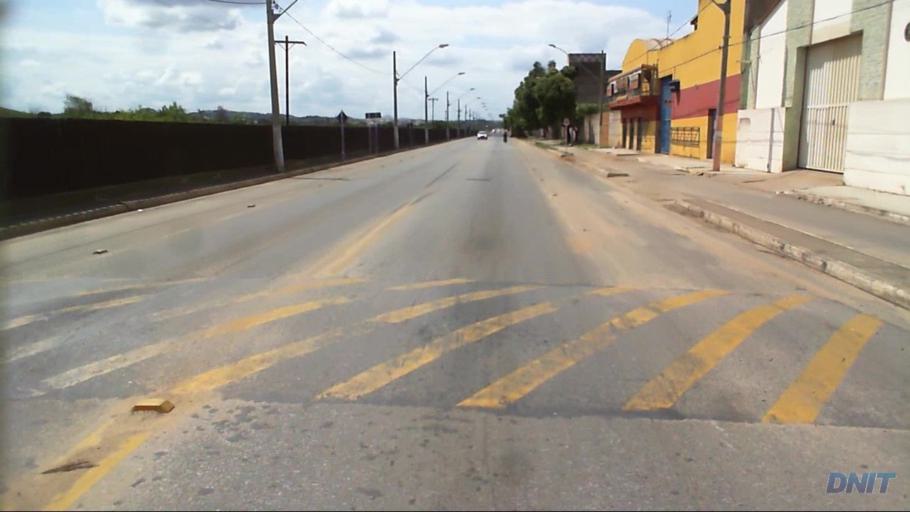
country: BR
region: Minas Gerais
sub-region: Governador Valadares
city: Governador Valadares
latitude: -18.9006
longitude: -41.9856
